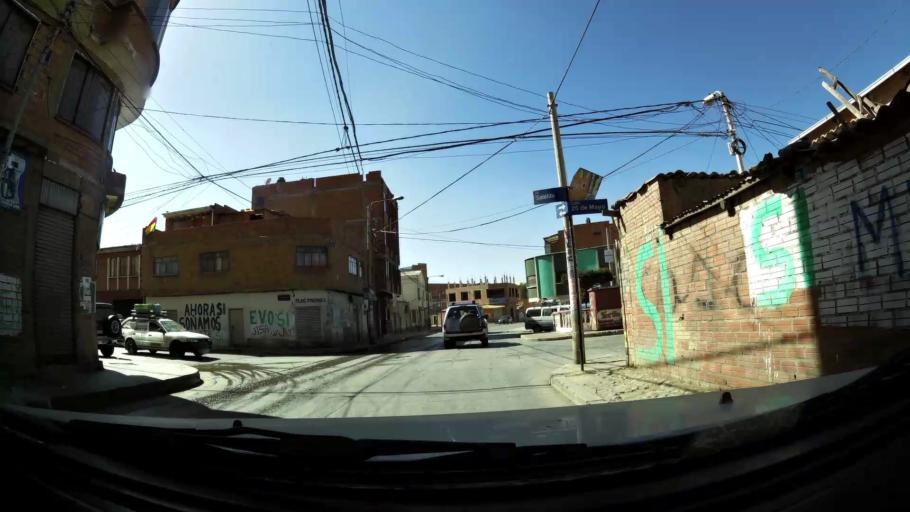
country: BO
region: La Paz
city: La Paz
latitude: -16.5178
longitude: -68.1629
